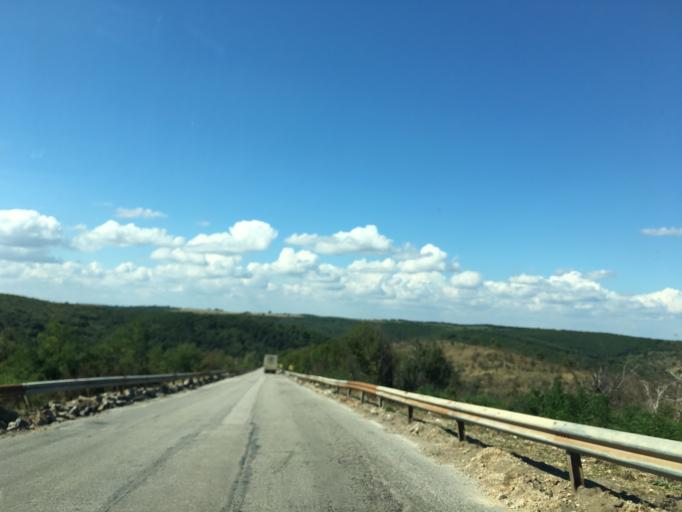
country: RO
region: Dolj
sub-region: Comuna Desa
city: Desa
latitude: 43.7591
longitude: 23.0013
